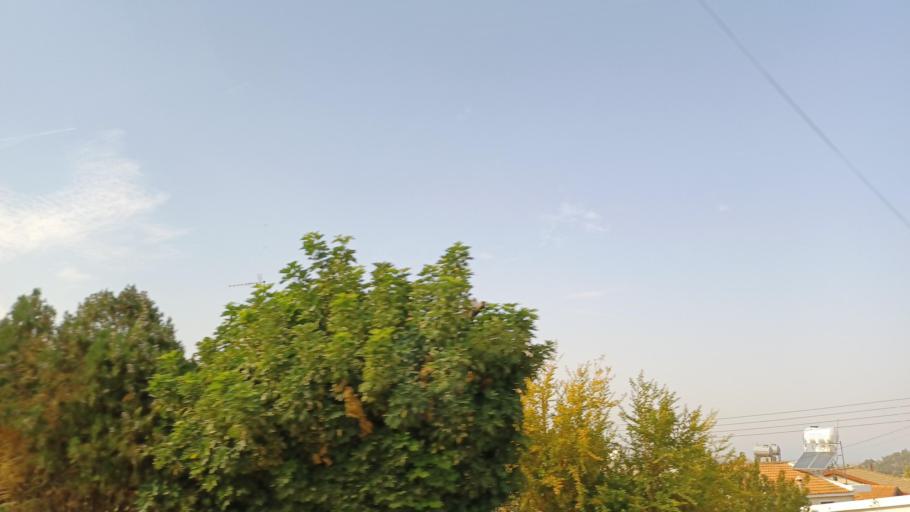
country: CY
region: Lefkosia
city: Kakopetria
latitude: 35.0392
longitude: 32.9033
